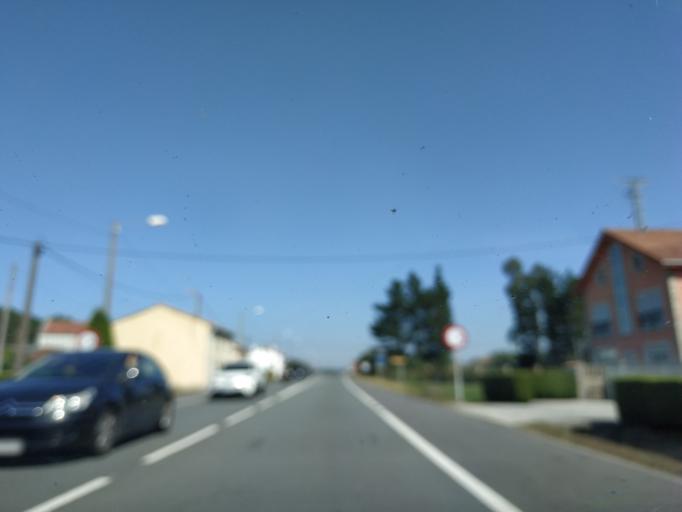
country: ES
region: Galicia
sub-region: Provincia da Coruna
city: Laracha
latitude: 43.2463
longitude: -8.6243
